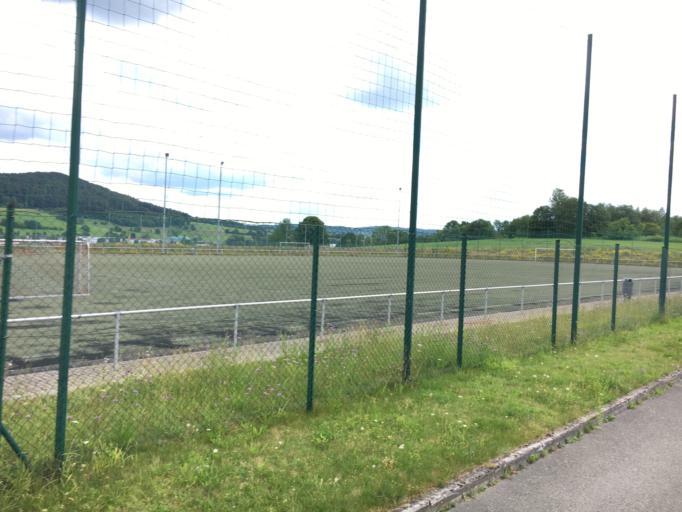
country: DE
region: Thuringia
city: Schmalkalden
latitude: 50.7265
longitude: 10.4755
